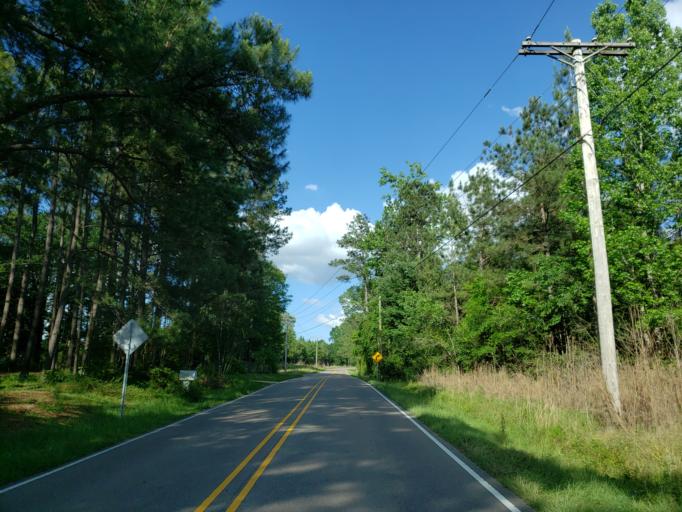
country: US
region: Mississippi
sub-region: Lamar County
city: West Hattiesburg
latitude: 31.2729
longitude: -89.3960
